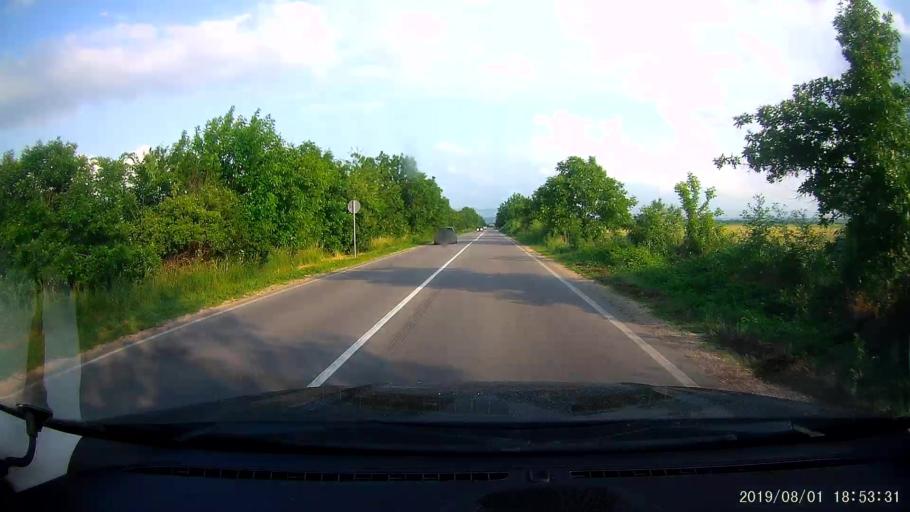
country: BG
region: Shumen
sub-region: Obshtina Shumen
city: Shumen
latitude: 43.2198
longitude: 26.9944
